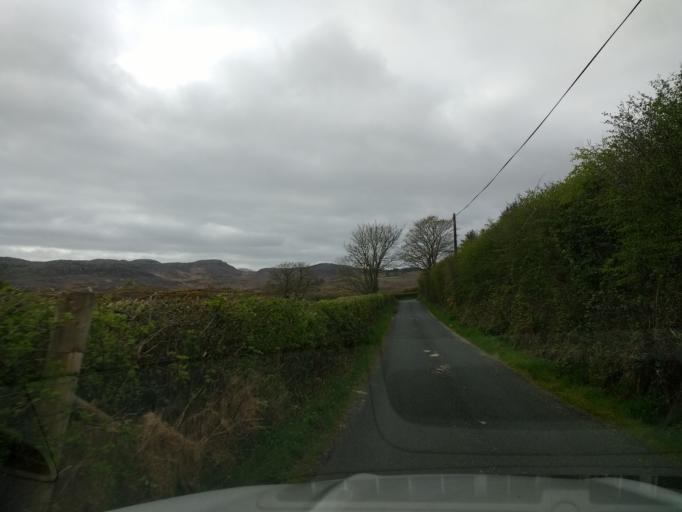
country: IE
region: Ulster
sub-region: County Donegal
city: Ramelton
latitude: 55.2518
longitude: -7.6371
